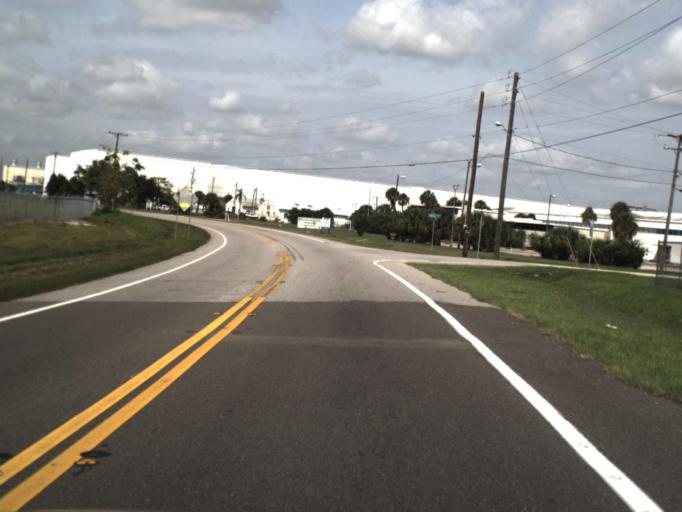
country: US
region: Florida
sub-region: Polk County
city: Auburndale
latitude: 28.0509
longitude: -81.7922
